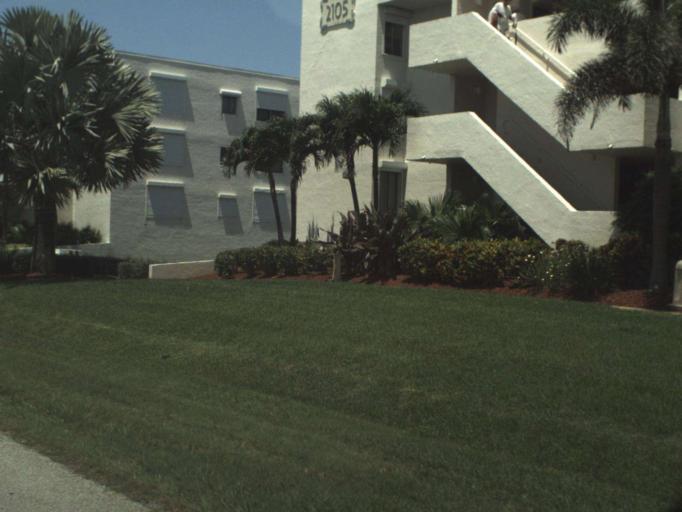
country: US
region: Florida
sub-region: Brevard County
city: Melbourne Beach
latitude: 28.0576
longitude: -80.5525
